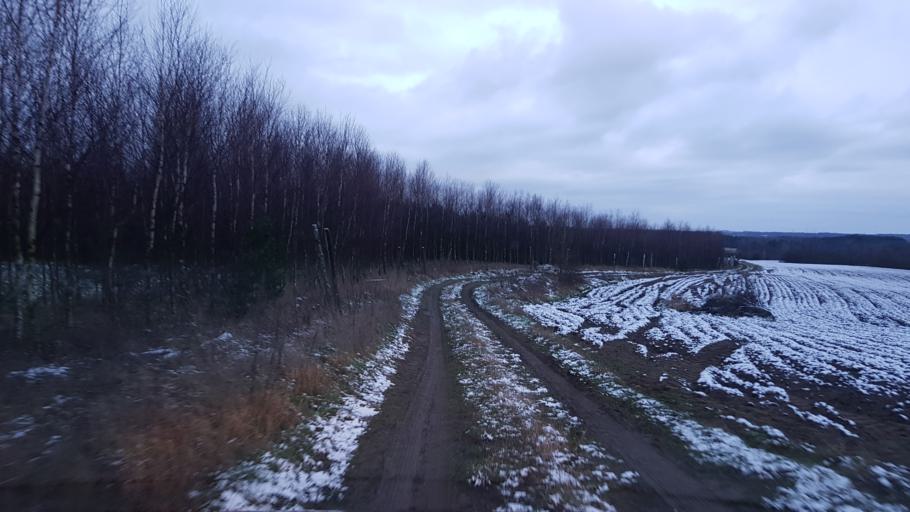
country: PL
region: Pomeranian Voivodeship
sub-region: Powiat bytowski
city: Tuchomie
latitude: 54.1511
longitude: 17.3049
